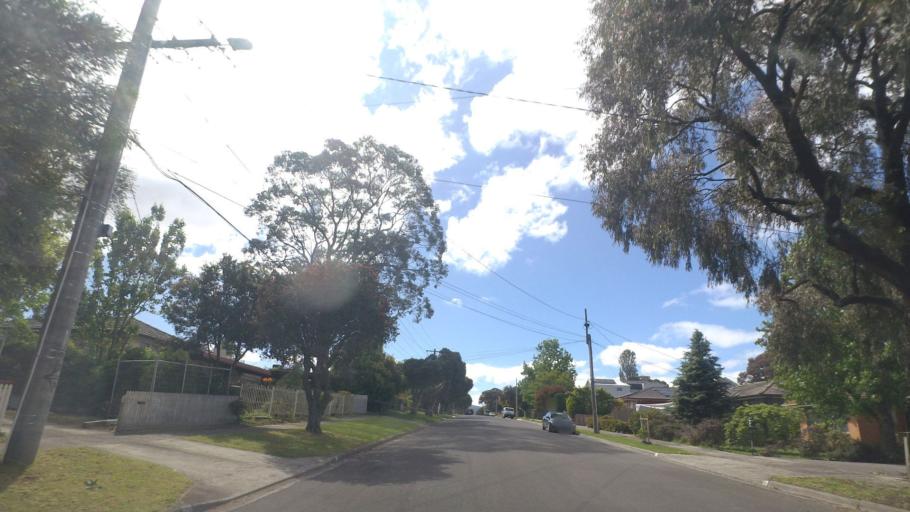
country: AU
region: Victoria
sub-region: Knox
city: Bayswater
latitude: -37.8532
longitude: 145.2707
